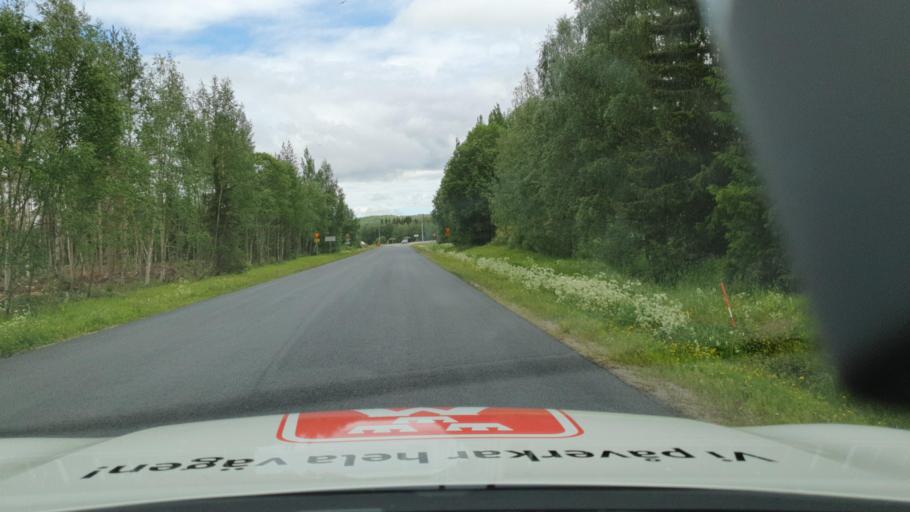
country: SE
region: Vaesterbotten
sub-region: Dorotea Kommun
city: Dorotea
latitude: 64.2519
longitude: 16.4834
